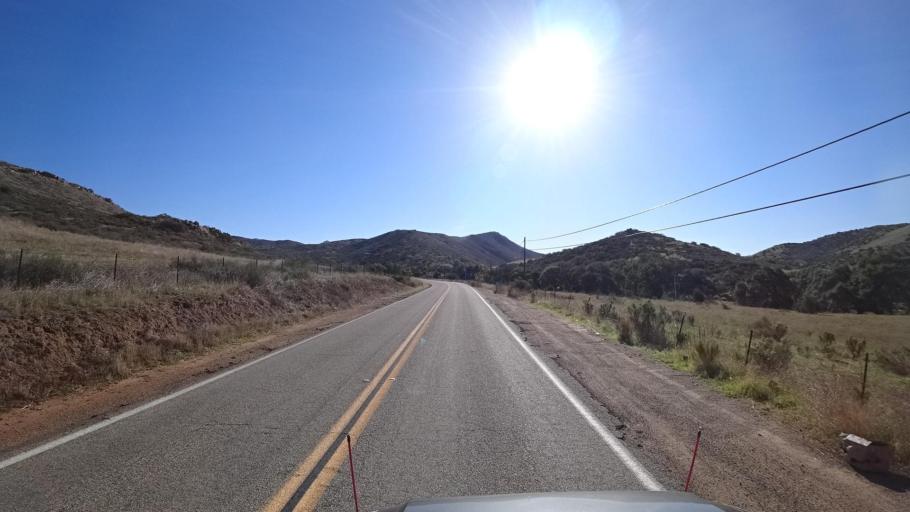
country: US
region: California
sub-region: San Diego County
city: Jamul
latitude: 32.6682
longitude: -116.8177
